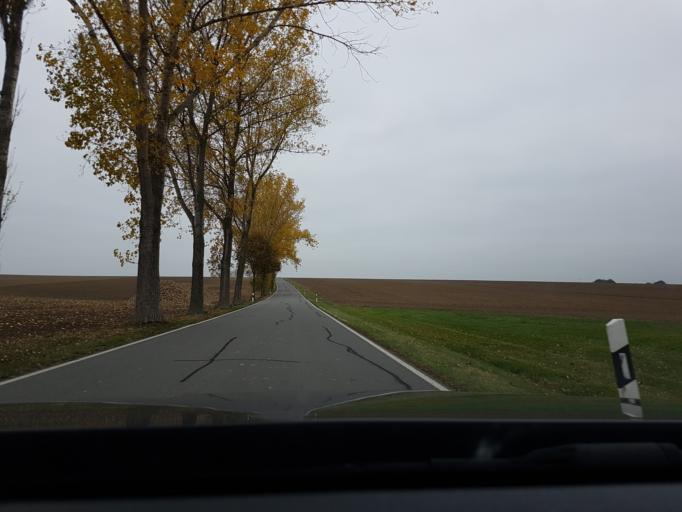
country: DE
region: Saxony
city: Altmittweida
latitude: 50.9706
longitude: 12.9539
